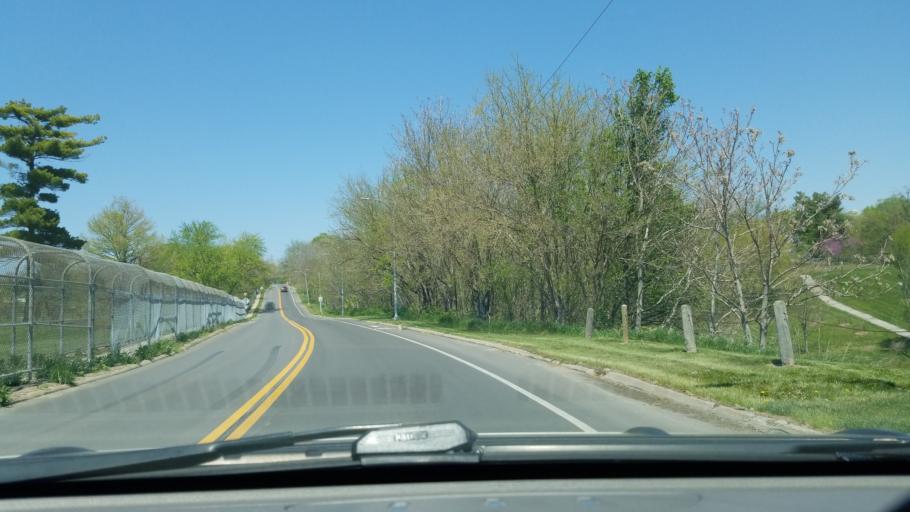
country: US
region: Nebraska
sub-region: Douglas County
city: Omaha
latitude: 41.2209
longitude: -95.9374
